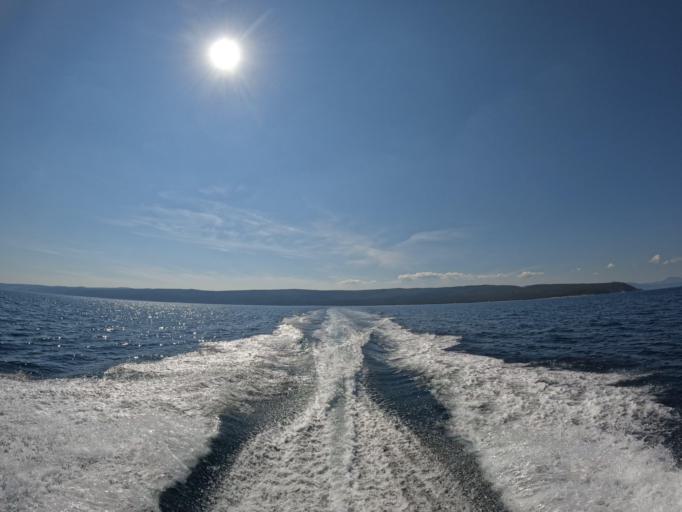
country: HR
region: Primorsko-Goranska
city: Cres
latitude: 44.9455
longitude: 14.5083
